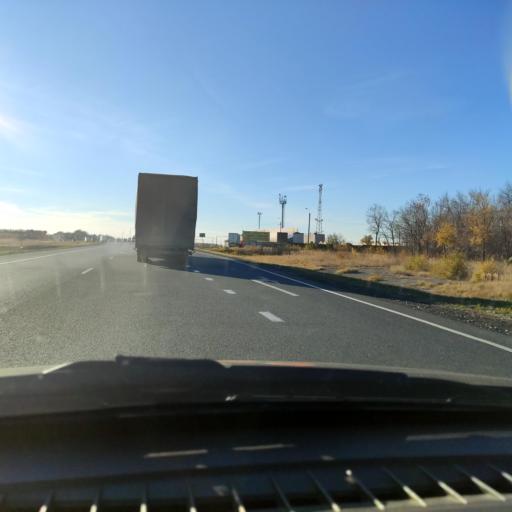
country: RU
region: Samara
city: Obsharovka
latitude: 53.2236
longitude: 48.8709
